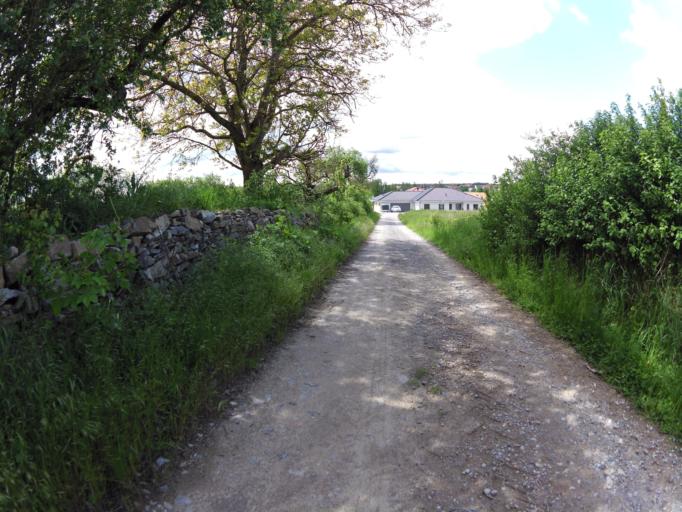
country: DE
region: Bavaria
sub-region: Regierungsbezirk Unterfranken
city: Volkach
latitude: 49.8709
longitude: 10.2337
